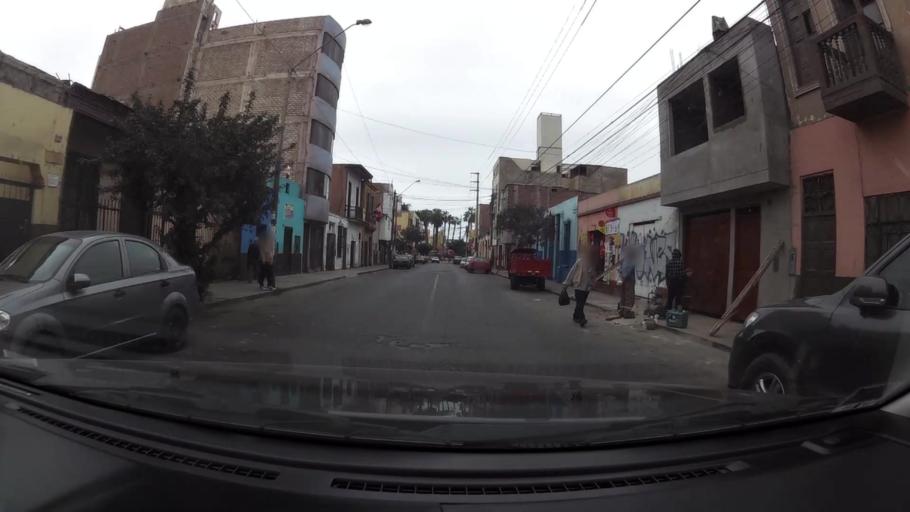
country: PE
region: Lima
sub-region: Lima
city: Surco
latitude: -12.1470
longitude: -77.0165
